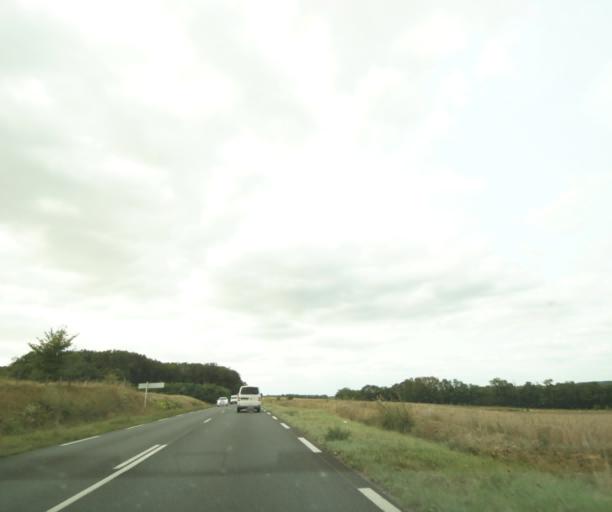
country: FR
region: Centre
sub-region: Departement d'Indre-et-Loire
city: Chambourg-sur-Indre
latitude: 47.1644
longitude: 0.9857
